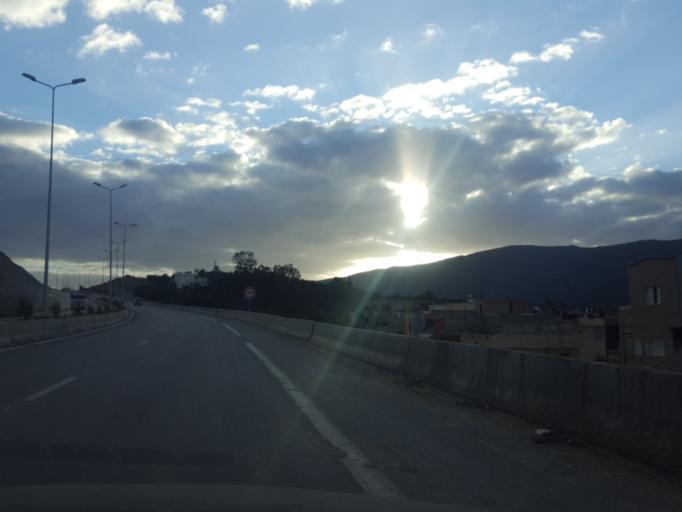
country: TN
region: Tunis
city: Hammam-Lif
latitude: 36.6984
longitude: 10.4004
